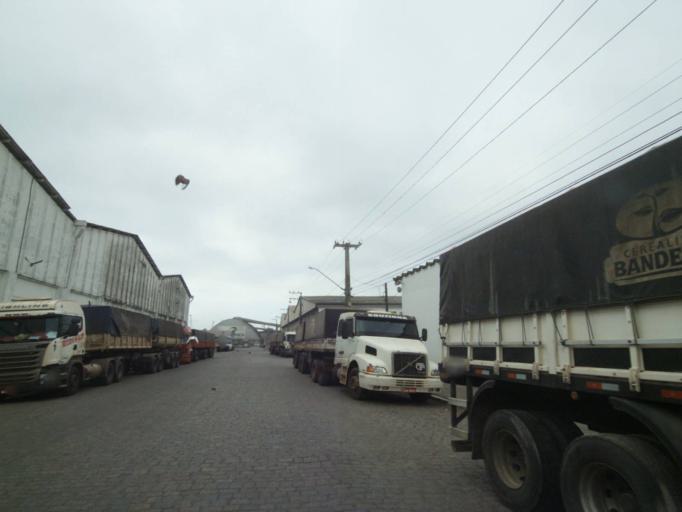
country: BR
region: Parana
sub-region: Paranagua
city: Paranagua
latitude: -25.5109
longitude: -48.5154
